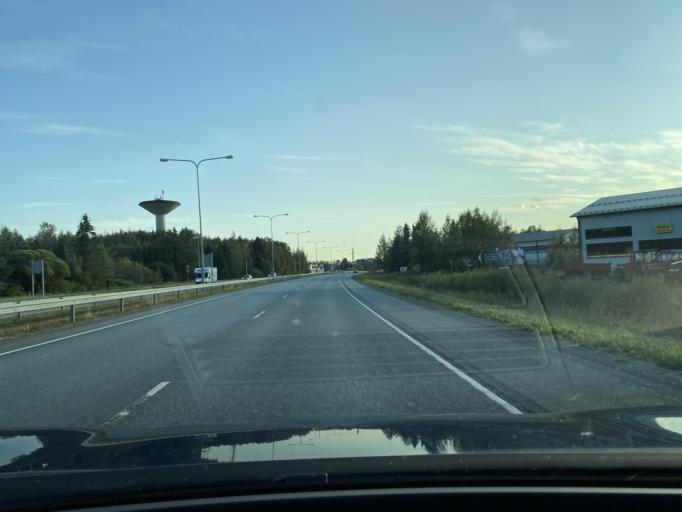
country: FI
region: Southern Ostrobothnia
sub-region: Seinaejoki
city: Nurmo
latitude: 62.8100
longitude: 22.8884
